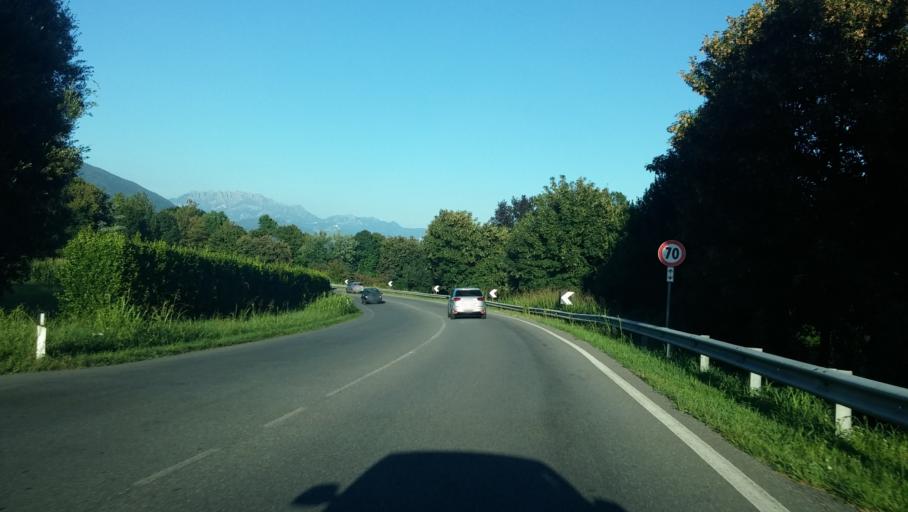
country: IT
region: Lombardy
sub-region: Provincia di Como
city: Vill'Albese
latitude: 45.7962
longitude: 9.2030
